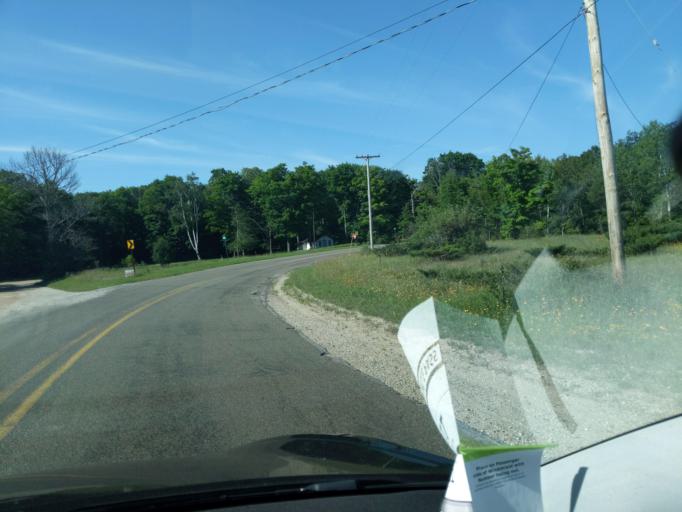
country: US
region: Michigan
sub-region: Mackinac County
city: Saint Ignace
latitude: 45.6996
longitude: -84.7316
